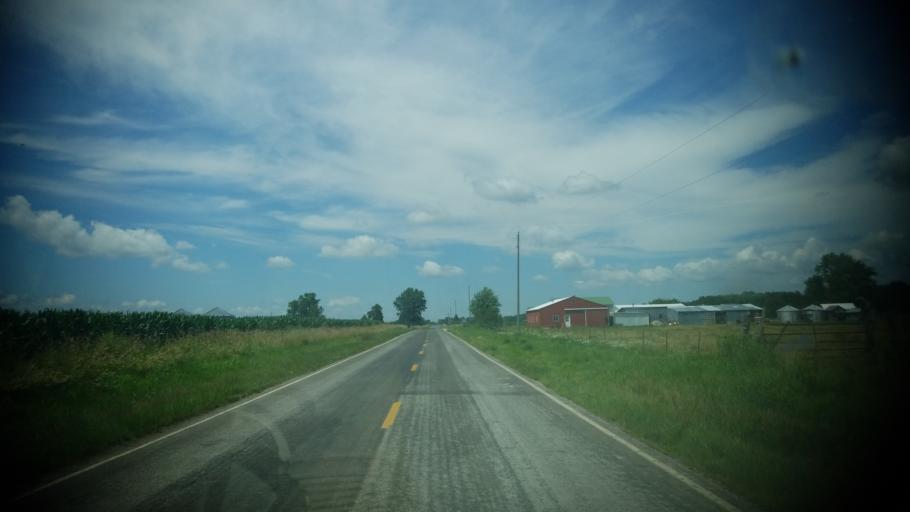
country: US
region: Missouri
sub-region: Audrain County
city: Vandalia
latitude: 39.3271
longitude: -91.3451
